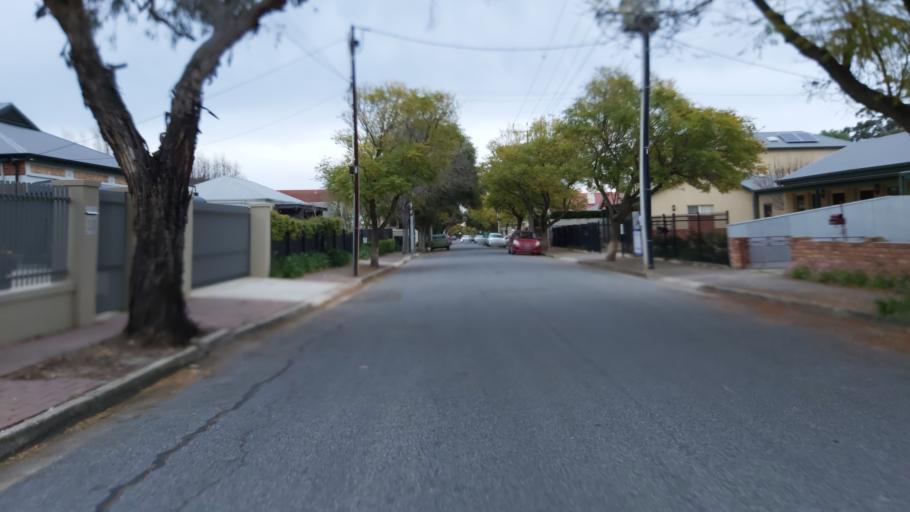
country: AU
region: South Australia
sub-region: Unley
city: Fullarton
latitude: -34.9514
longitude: 138.6208
